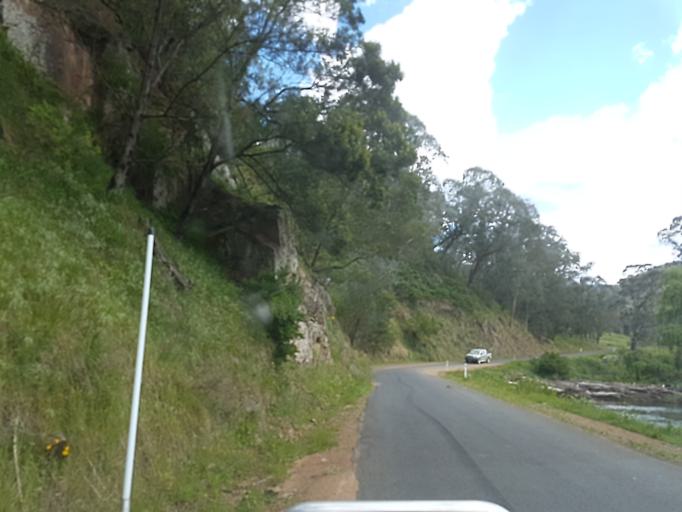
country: AU
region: Victoria
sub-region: East Gippsland
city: Bairnsdale
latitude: -37.4300
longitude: 147.2512
